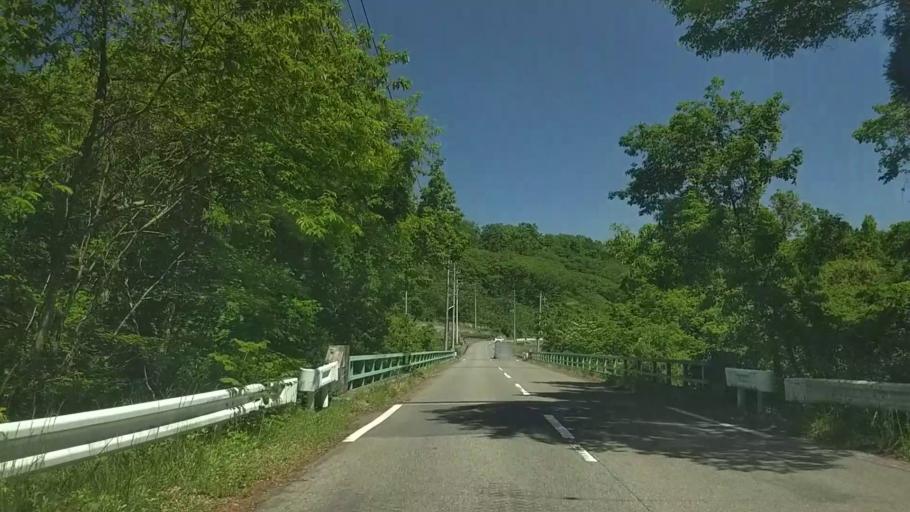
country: JP
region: Yamanashi
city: Nirasaki
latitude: 35.8550
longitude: 138.4330
